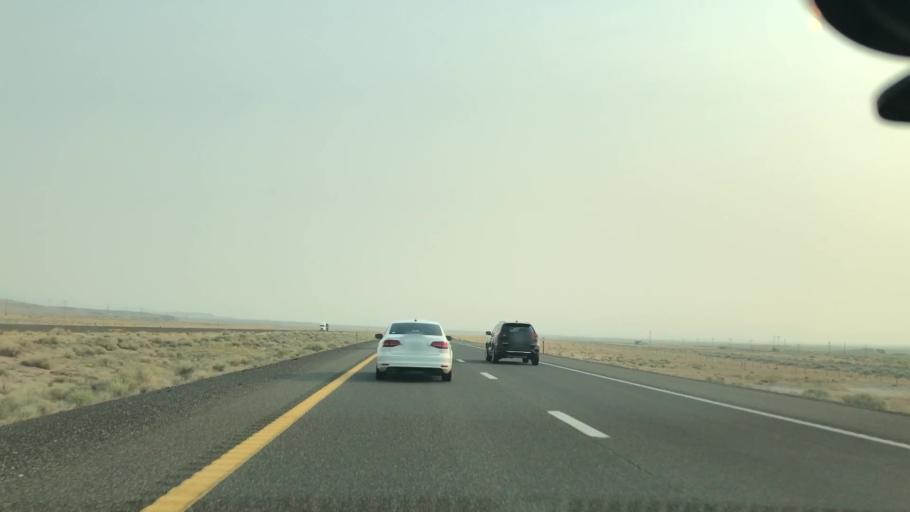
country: US
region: Nevada
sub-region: Pershing County
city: Lovelock
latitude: 40.0130
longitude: -118.6769
